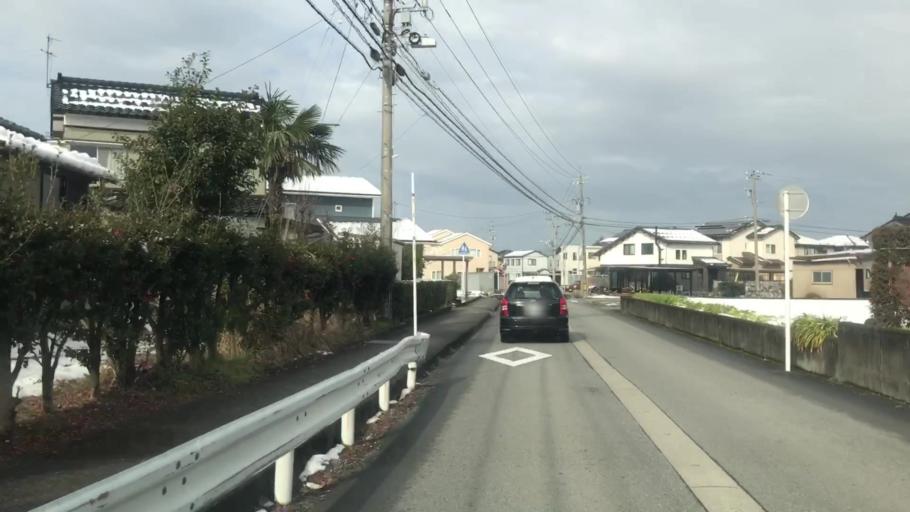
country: JP
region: Toyama
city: Toyama-shi
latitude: 36.6487
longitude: 137.2283
